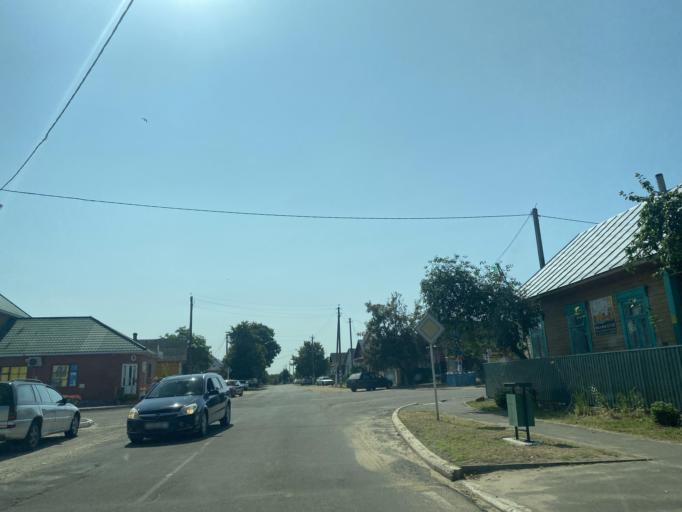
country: BY
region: Brest
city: Ivanava
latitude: 52.3153
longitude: 25.6123
